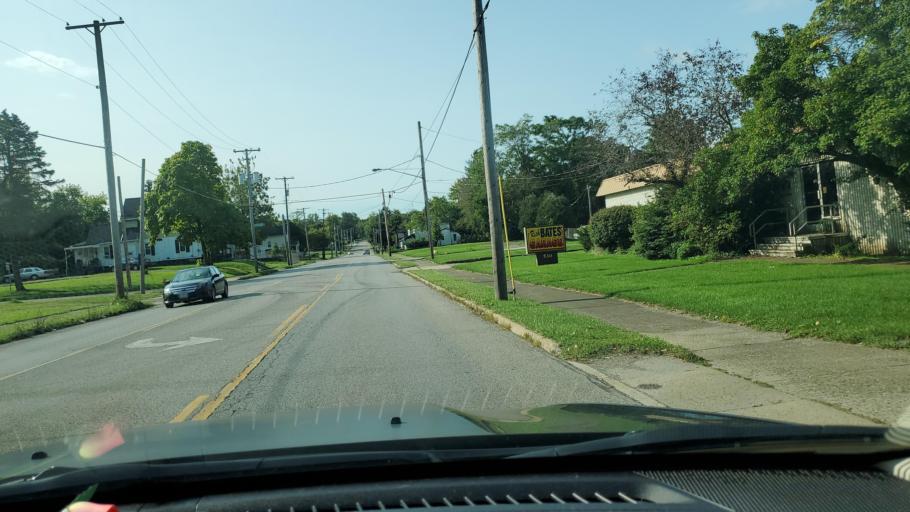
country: US
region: Ohio
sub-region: Mahoning County
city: Youngstown
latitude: 41.0942
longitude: -80.6712
